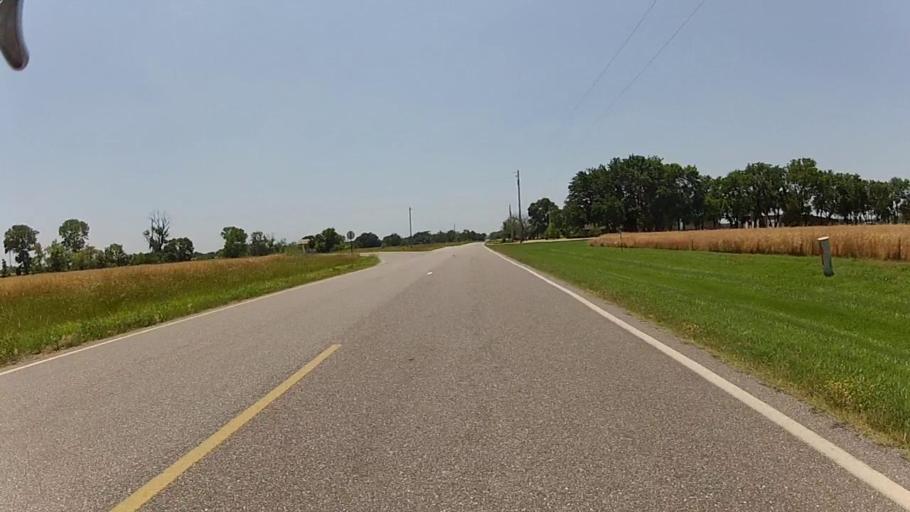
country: US
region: Kansas
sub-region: Montgomery County
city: Cherryvale
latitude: 37.2534
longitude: -95.5370
